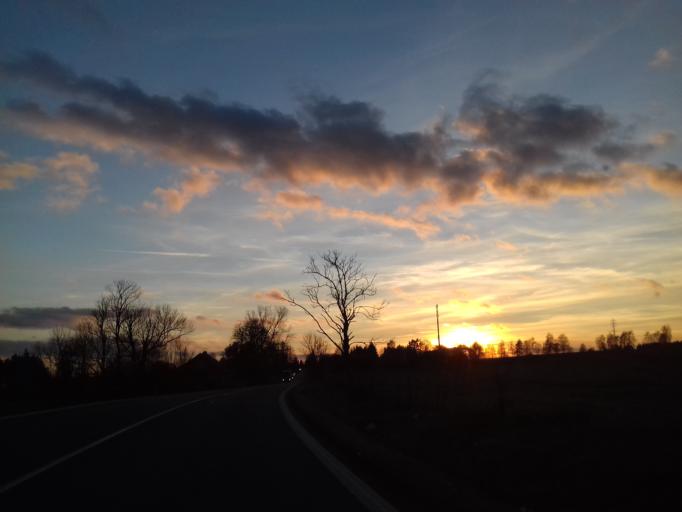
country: CZ
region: Vysocina
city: Krizova
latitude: 49.7127
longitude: 15.8522
